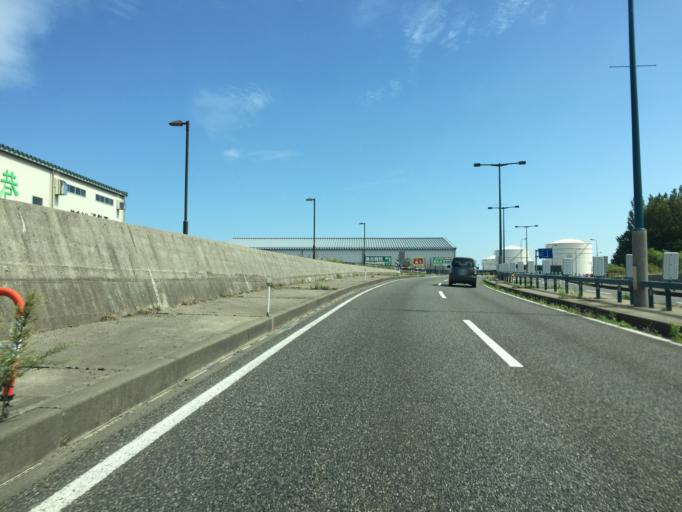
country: JP
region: Niigata
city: Niigata-shi
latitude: 37.9474
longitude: 139.0790
